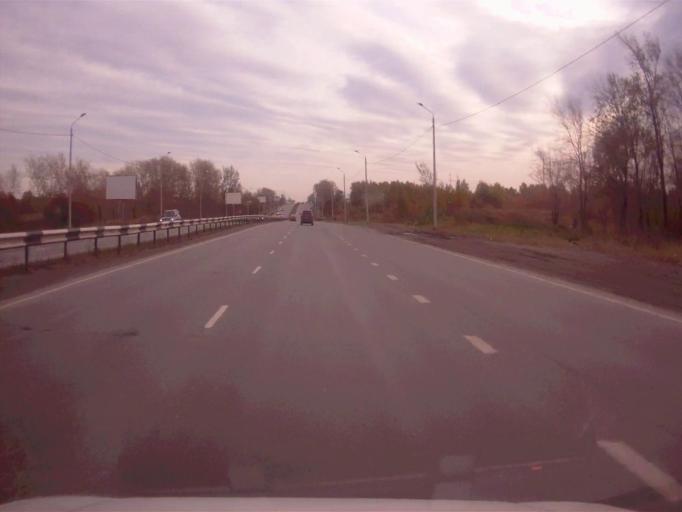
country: RU
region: Chelyabinsk
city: Novosineglazovskiy
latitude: 55.0599
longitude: 61.4024
